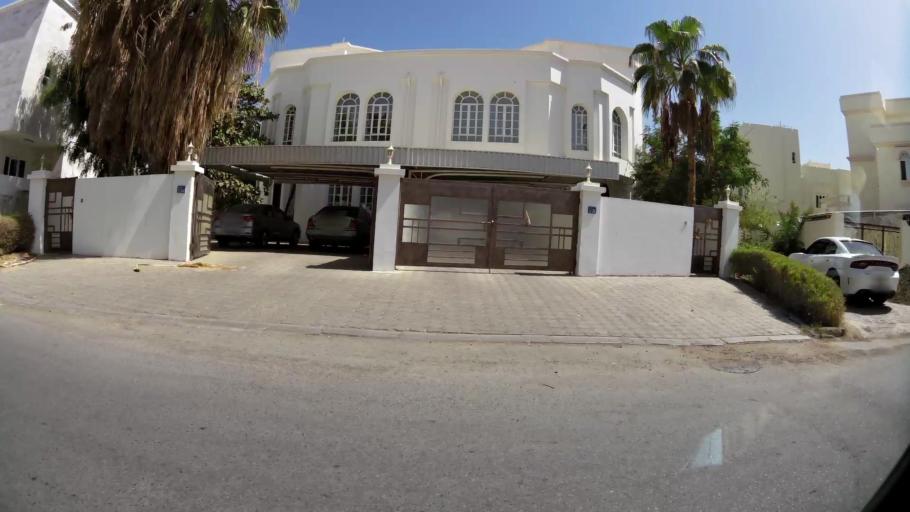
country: OM
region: Muhafazat Masqat
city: Bawshar
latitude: 23.5953
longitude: 58.4046
